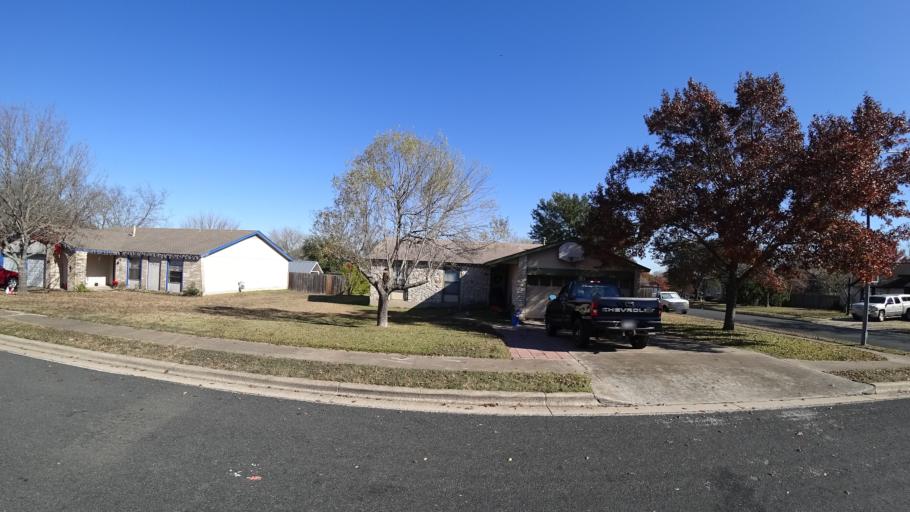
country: US
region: Texas
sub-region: Travis County
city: Wells Branch
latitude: 30.4234
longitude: -97.6880
